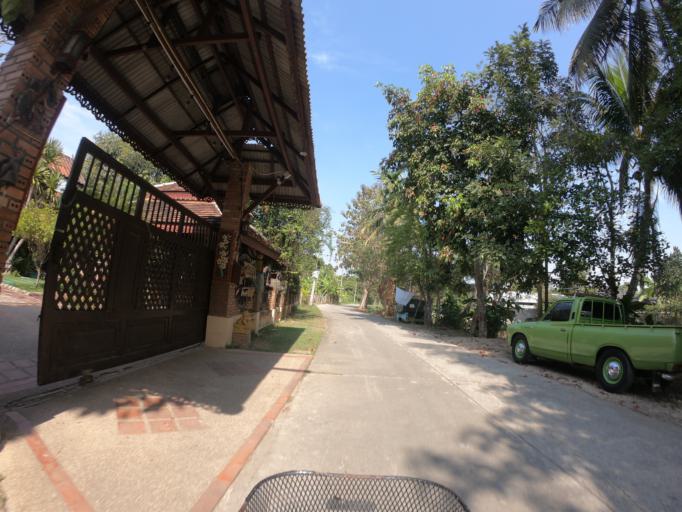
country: TH
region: Chiang Mai
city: Saraphi
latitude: 18.7047
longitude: 99.0596
